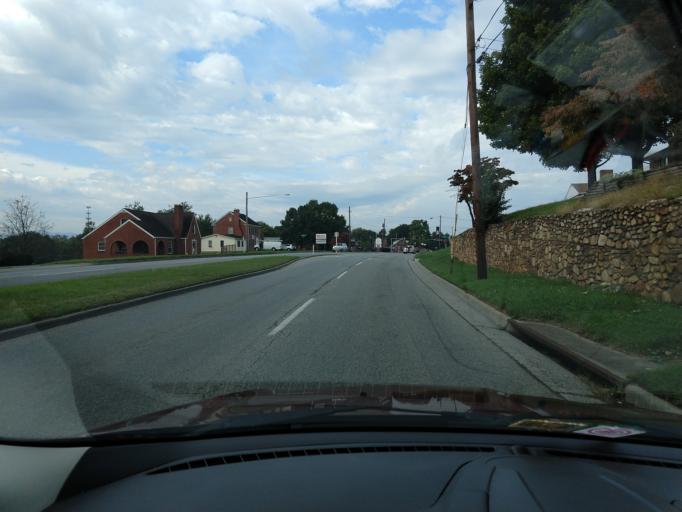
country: US
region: Virginia
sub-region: Roanoke County
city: Vinton
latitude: 37.2778
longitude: -79.8795
